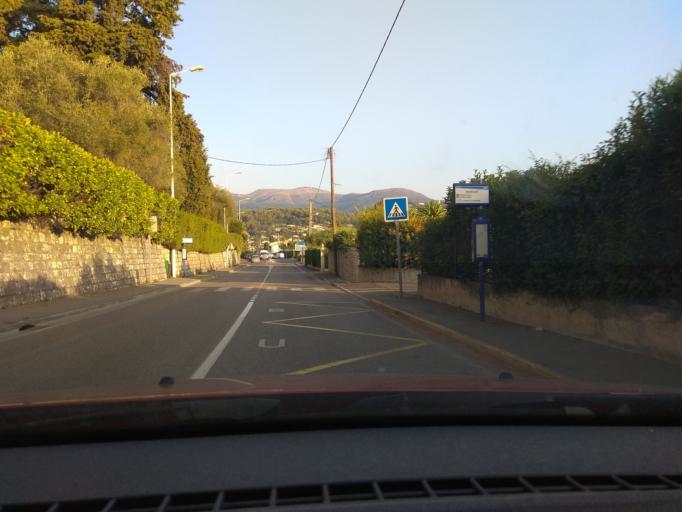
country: FR
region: Provence-Alpes-Cote d'Azur
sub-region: Departement des Alpes-Maritimes
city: La Colle-sur-Loup
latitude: 43.6827
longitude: 7.1124
